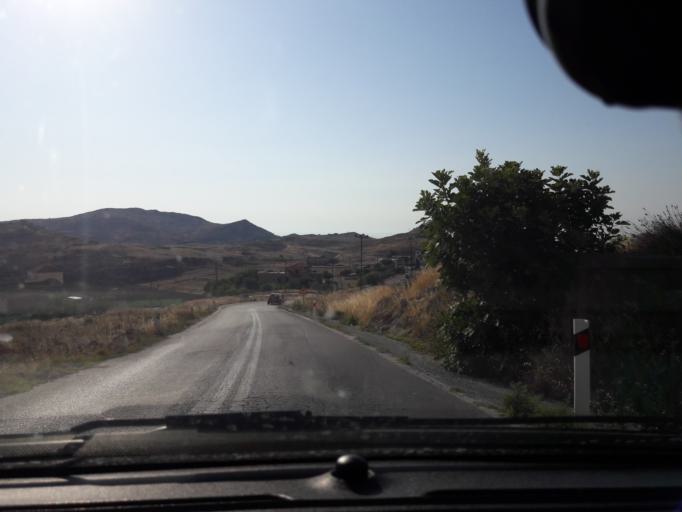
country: GR
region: North Aegean
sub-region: Nomos Lesvou
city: Myrina
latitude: 39.8635
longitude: 25.0765
